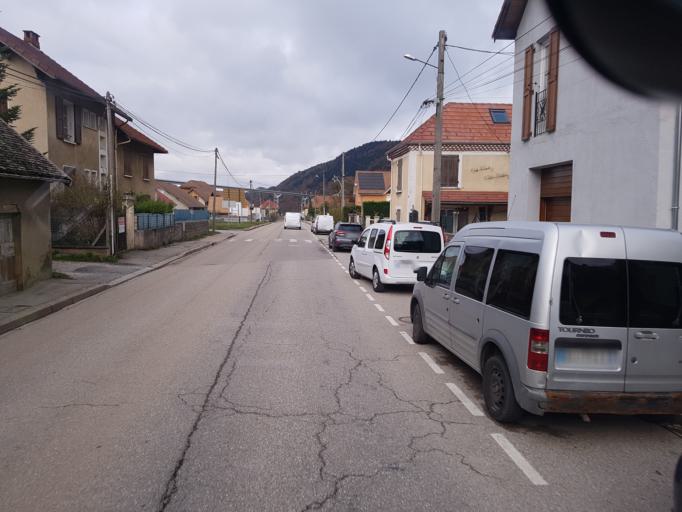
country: FR
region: Rhone-Alpes
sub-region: Departement de l'Isere
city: La Motte-Saint-Martin
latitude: 44.9229
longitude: 5.6371
